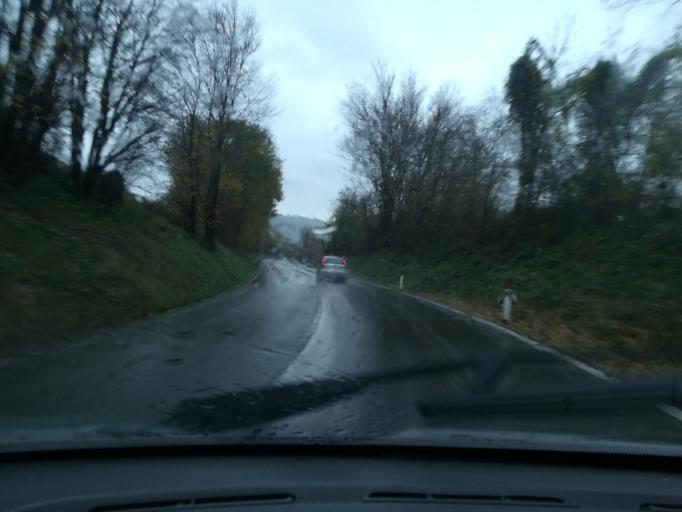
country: IT
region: The Marches
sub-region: Provincia di Macerata
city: Sforzacosta
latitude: 43.2637
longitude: 13.4207
